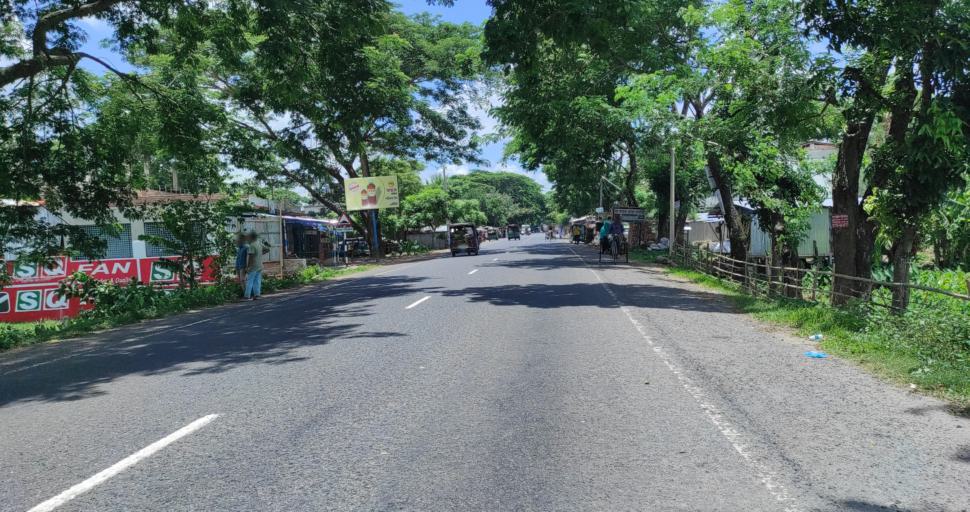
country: BD
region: Barisal
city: Barisal
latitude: 22.8185
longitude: 90.2718
